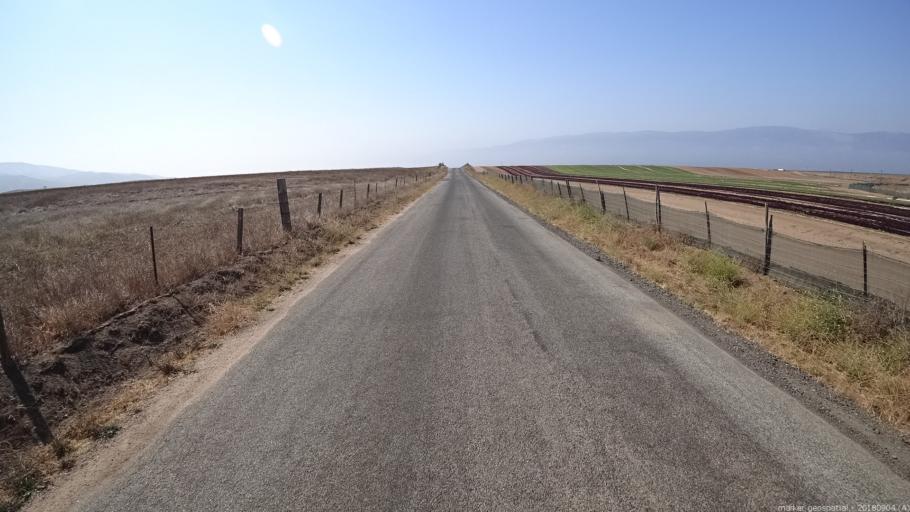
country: US
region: California
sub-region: Monterey County
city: Gonzales
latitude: 36.5101
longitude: -121.3650
